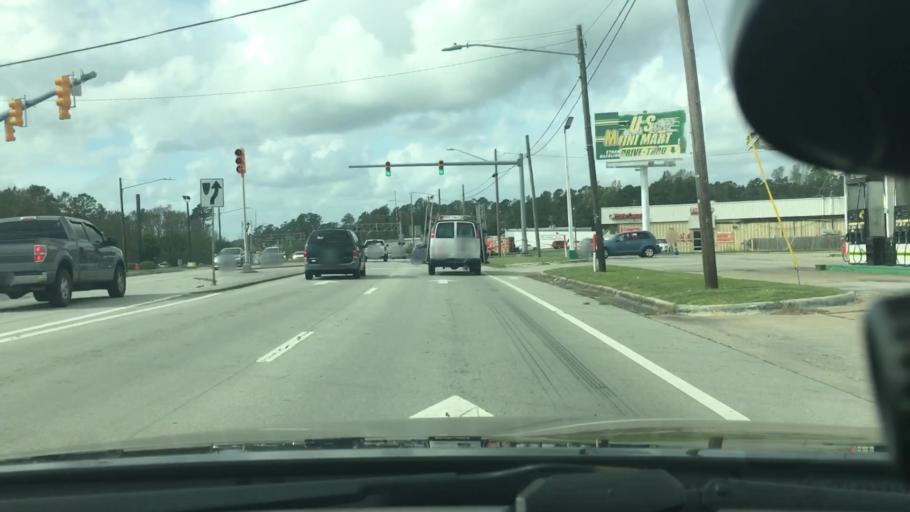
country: US
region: North Carolina
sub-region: Craven County
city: Havelock
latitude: 34.8796
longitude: -76.9055
